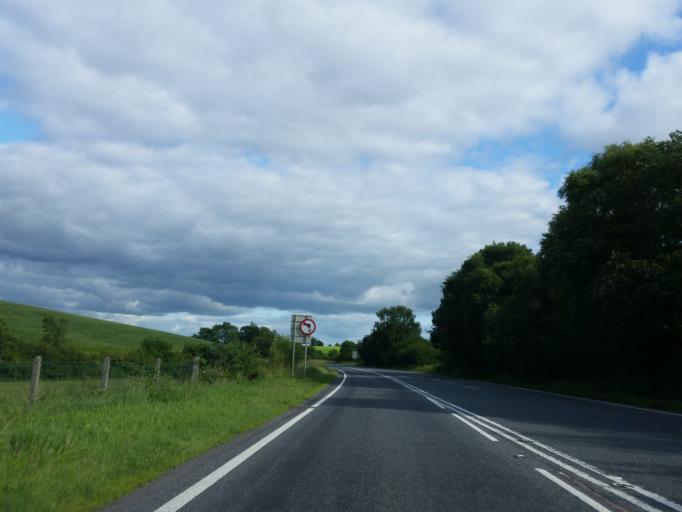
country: GB
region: Northern Ireland
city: Lisnaskea
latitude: 54.3077
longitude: -7.4921
